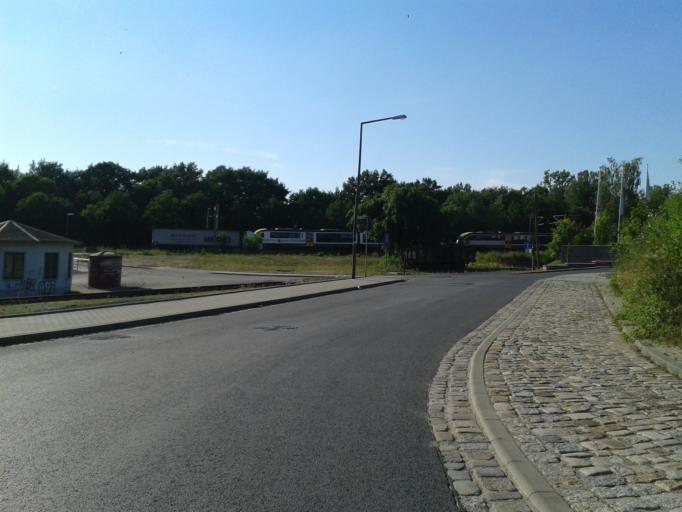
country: DE
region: Saxony
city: Albertstadt
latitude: 51.0901
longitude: 13.7672
